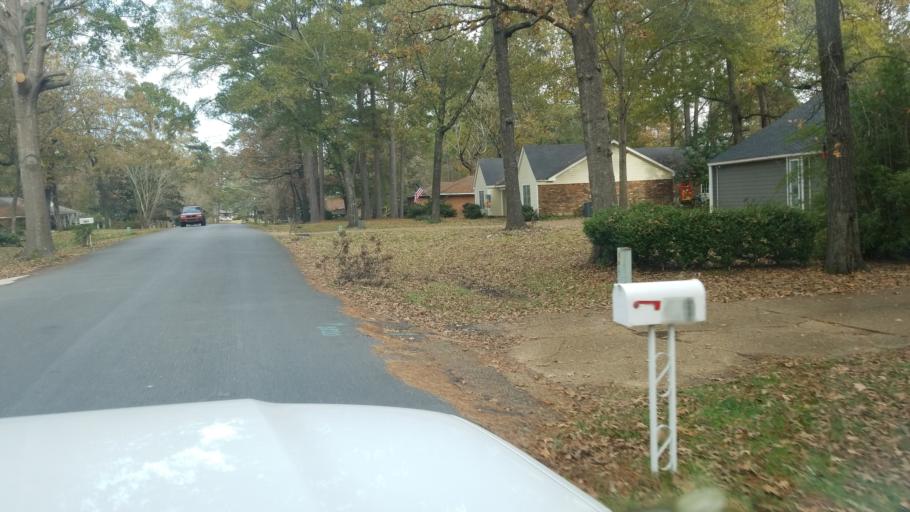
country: US
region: Mississippi
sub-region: Madison County
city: Ridgeland
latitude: 32.3865
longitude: -90.0316
